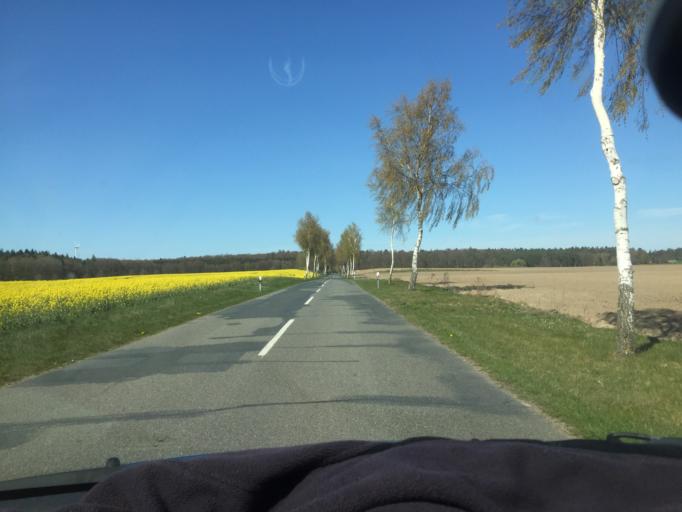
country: DE
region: Lower Saxony
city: Nahrendorf
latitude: 53.1820
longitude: 10.8160
